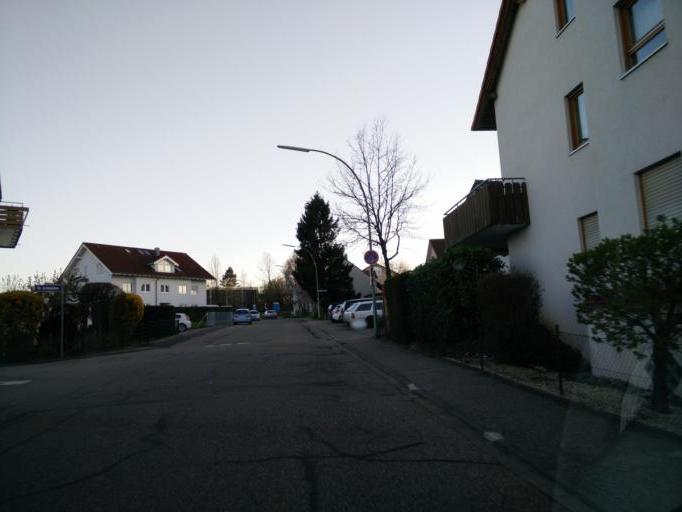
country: DE
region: Baden-Wuerttemberg
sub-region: Karlsruhe Region
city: Birkenfeld
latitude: 48.8578
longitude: 8.6563
